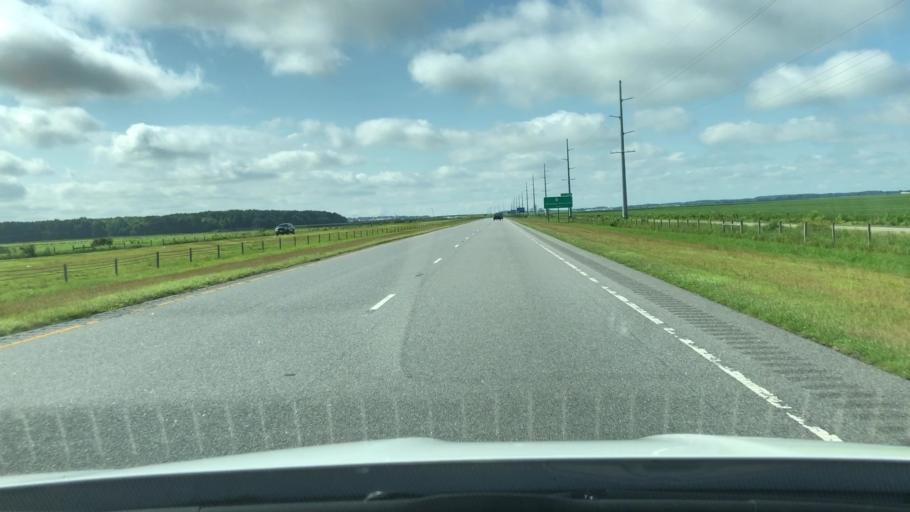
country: US
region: North Carolina
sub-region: Pasquotank County
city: Elizabeth City
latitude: 36.3117
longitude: -76.3074
